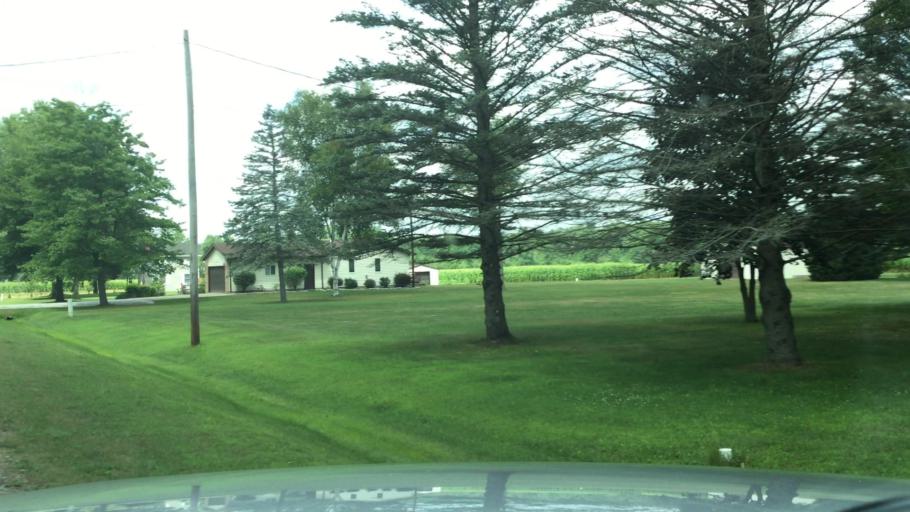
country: US
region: Michigan
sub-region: Saginaw County
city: Birch Run
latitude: 43.3073
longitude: -83.8238
